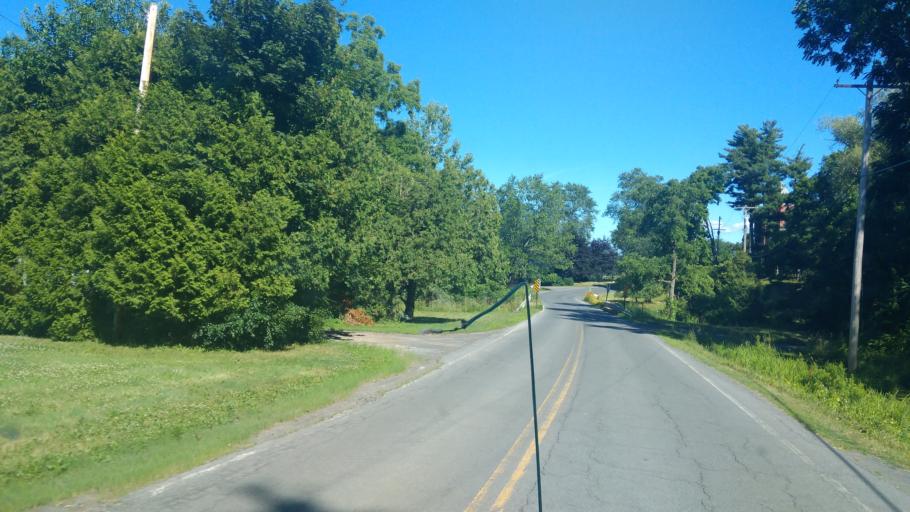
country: US
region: New York
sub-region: Seneca County
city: Seneca Falls
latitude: 42.9921
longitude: -76.8039
